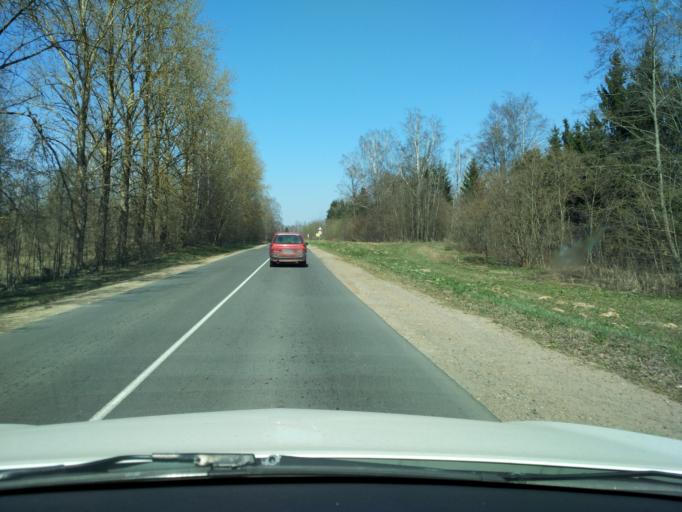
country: BY
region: Minsk
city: Slabada
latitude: 53.9852
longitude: 27.9567
